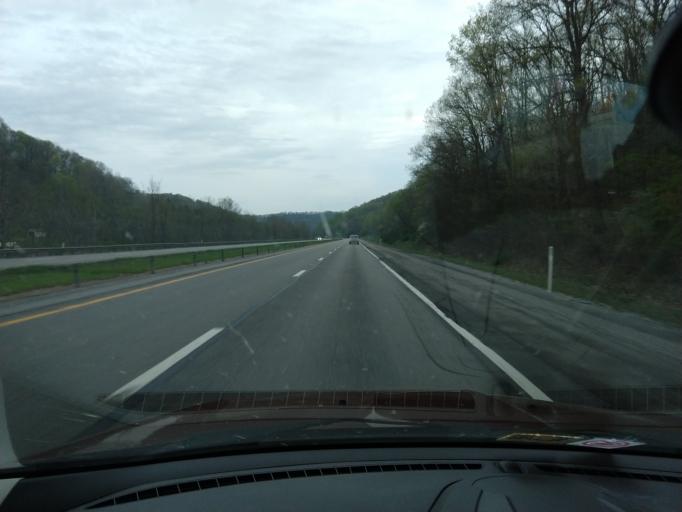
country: US
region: West Virginia
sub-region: Lewis County
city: Weston
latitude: 38.9952
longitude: -80.5050
